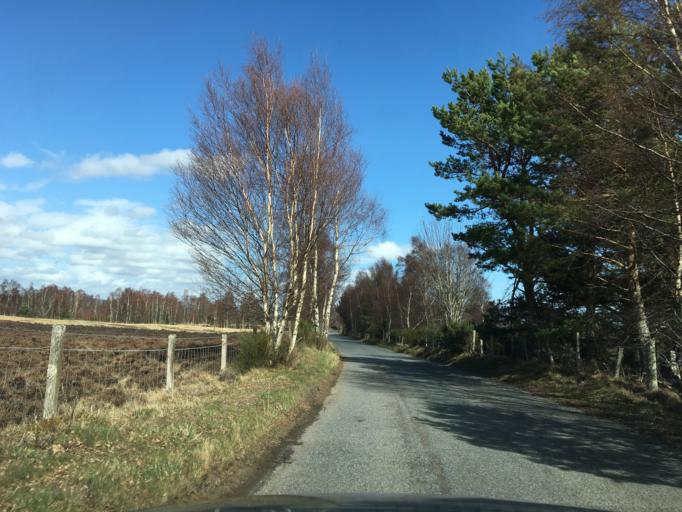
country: GB
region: Scotland
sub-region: Highland
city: Aviemore
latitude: 57.2022
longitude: -3.7960
